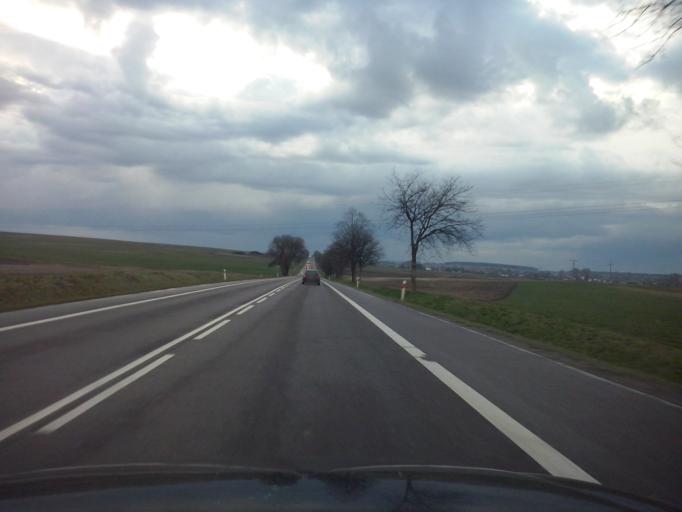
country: PL
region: Lublin Voivodeship
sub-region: Chelm
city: Chelm
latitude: 51.1657
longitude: 23.3783
